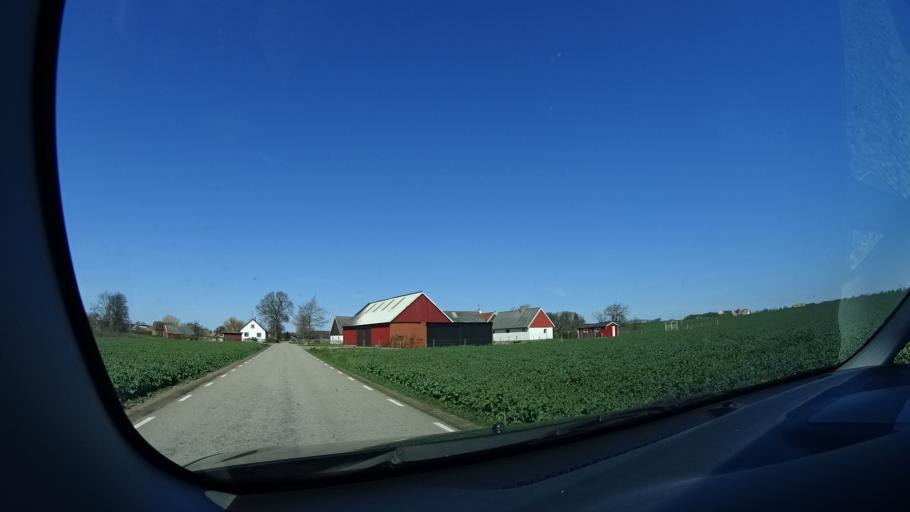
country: SE
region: Skane
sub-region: Hoganas Kommun
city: Hoganas
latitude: 56.2473
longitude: 12.5700
